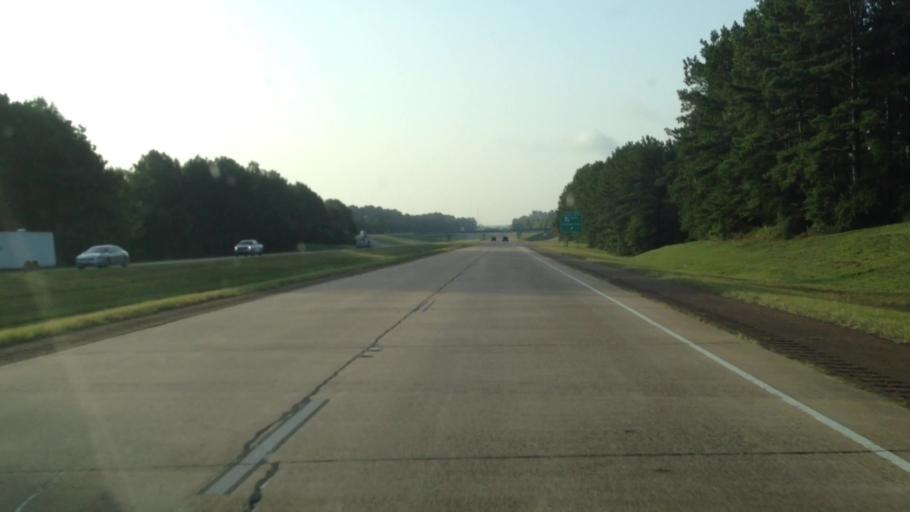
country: US
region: Louisiana
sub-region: Rapides Parish
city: Boyce
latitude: 31.4138
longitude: -92.7232
